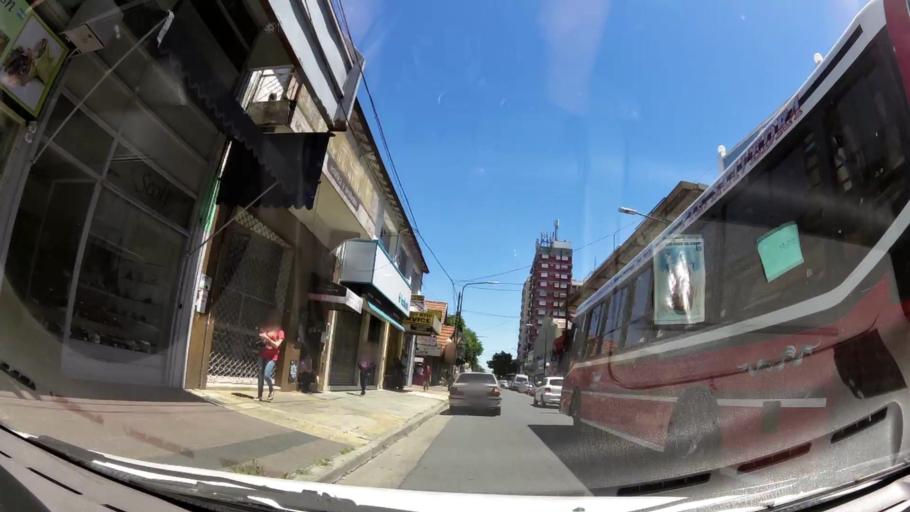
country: AR
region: Buenos Aires
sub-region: Partido de San Isidro
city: San Isidro
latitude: -34.4897
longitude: -58.5008
